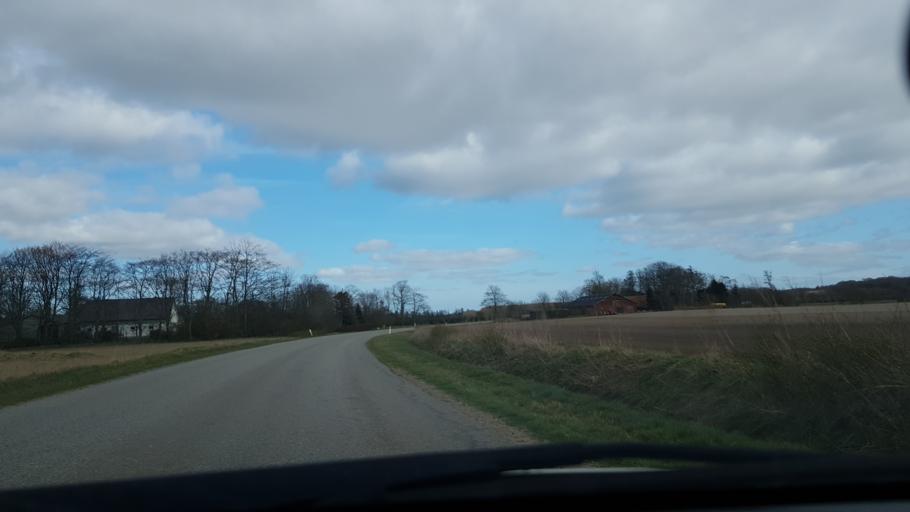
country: DK
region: South Denmark
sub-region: Vejen Kommune
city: Brorup
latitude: 55.4376
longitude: 9.0278
